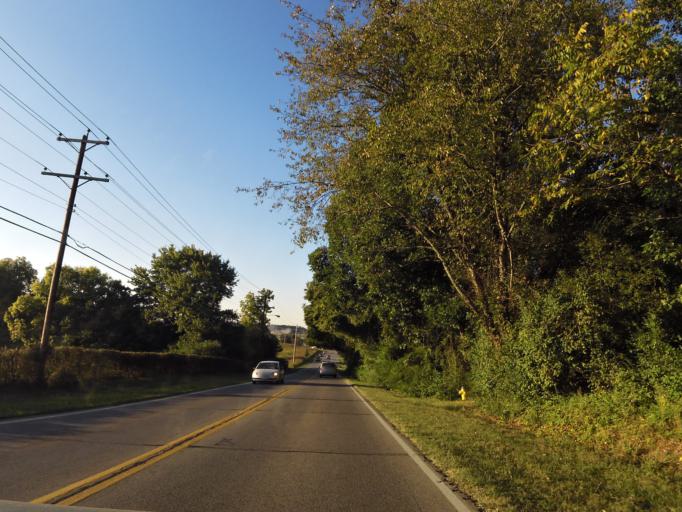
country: US
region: Tennessee
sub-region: Blount County
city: Alcoa
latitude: 35.8107
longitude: -83.9768
